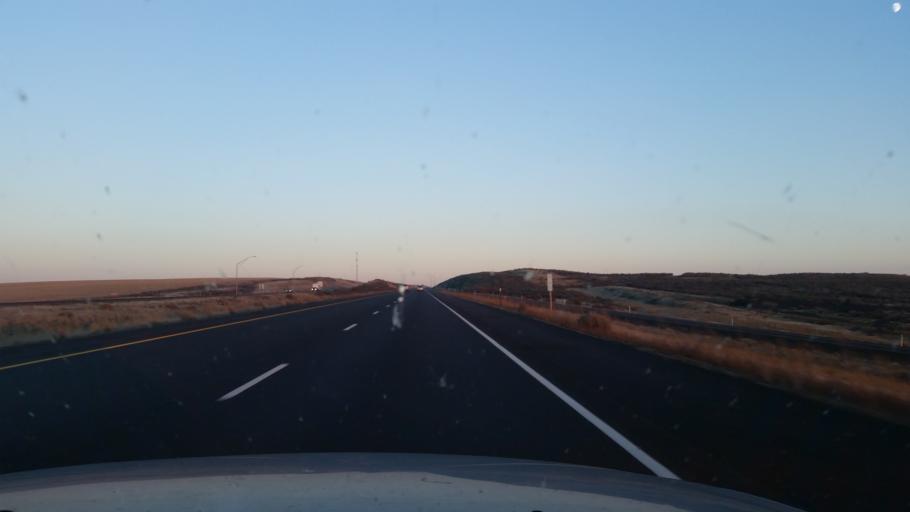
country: US
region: Washington
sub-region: Grant County
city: Warden
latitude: 47.0869
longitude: -118.8741
